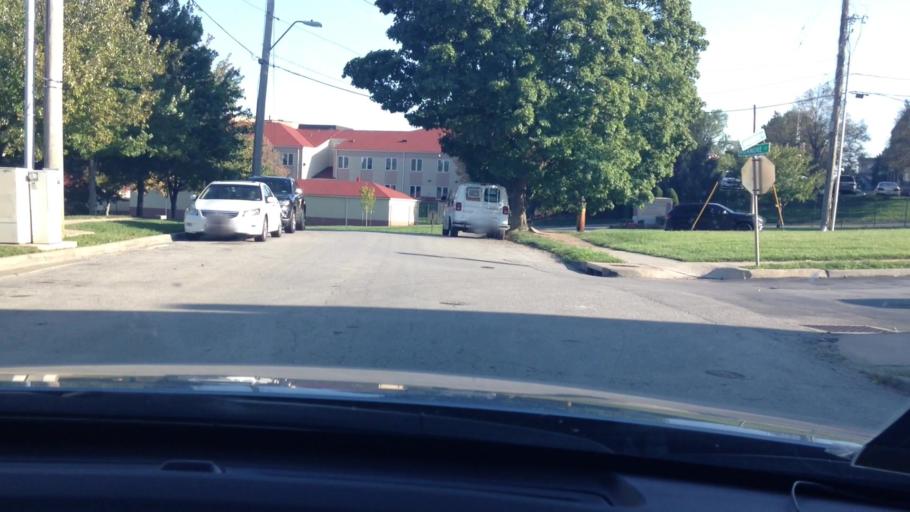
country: US
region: Kansas
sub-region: Johnson County
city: Westwood
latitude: 39.0501
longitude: -94.5964
